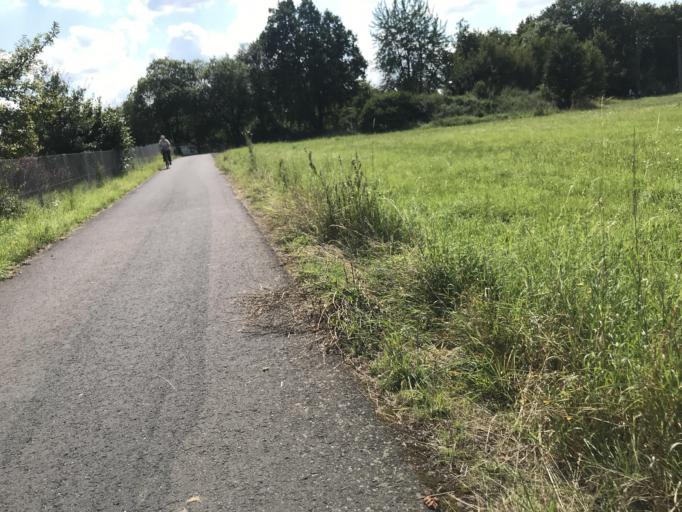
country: DE
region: Hesse
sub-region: Regierungsbezirk Giessen
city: Hungen
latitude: 50.4604
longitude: 8.9117
